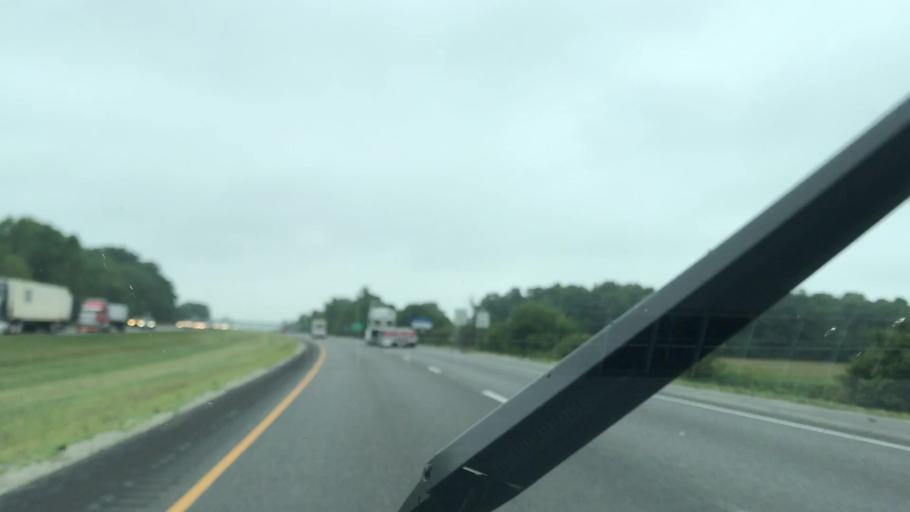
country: US
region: Indiana
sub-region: Boone County
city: Thorntown
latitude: 40.1347
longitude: -86.5204
